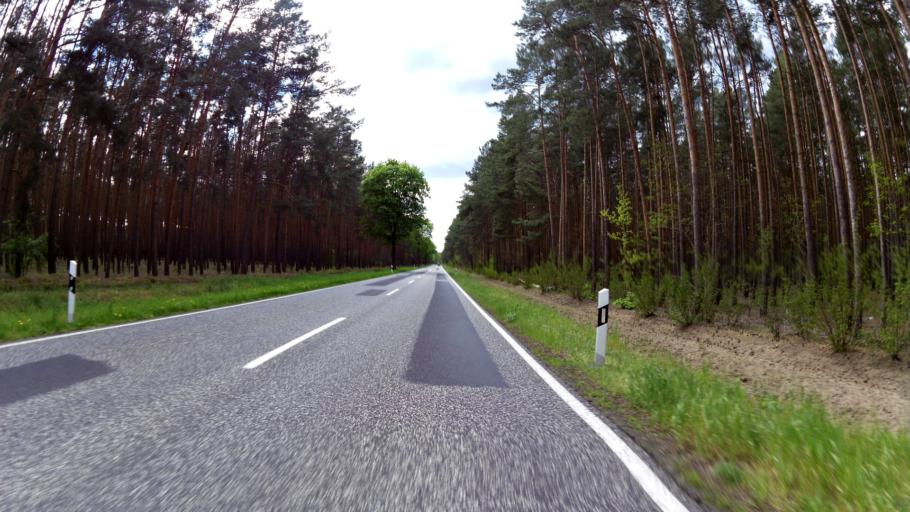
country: DE
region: Brandenburg
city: Spreenhagen
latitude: 52.3228
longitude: 13.9159
